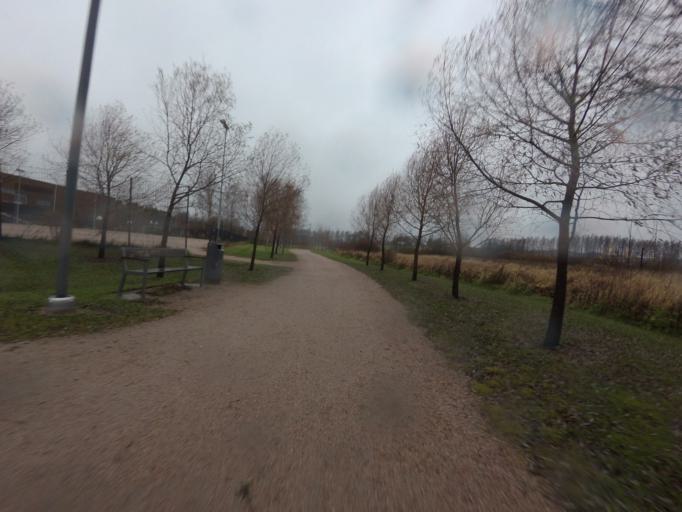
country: FI
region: Uusimaa
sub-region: Helsinki
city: Espoo
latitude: 60.2102
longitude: 24.6668
